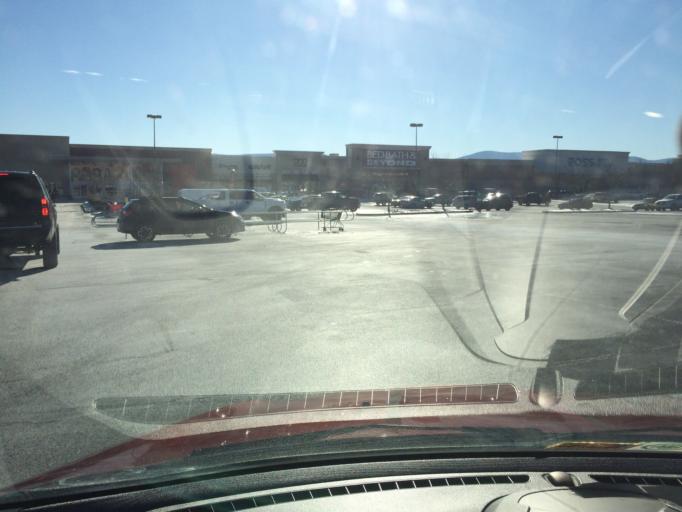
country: US
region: Virginia
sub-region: Augusta County
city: Lyndhurst
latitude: 38.0569
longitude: -78.9432
